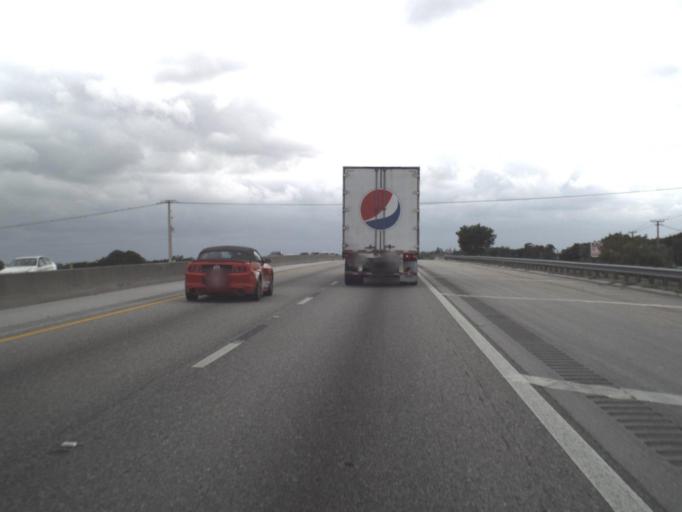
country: US
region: Florida
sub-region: Palm Beach County
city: Greenacres City
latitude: 26.5922
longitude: -80.1735
